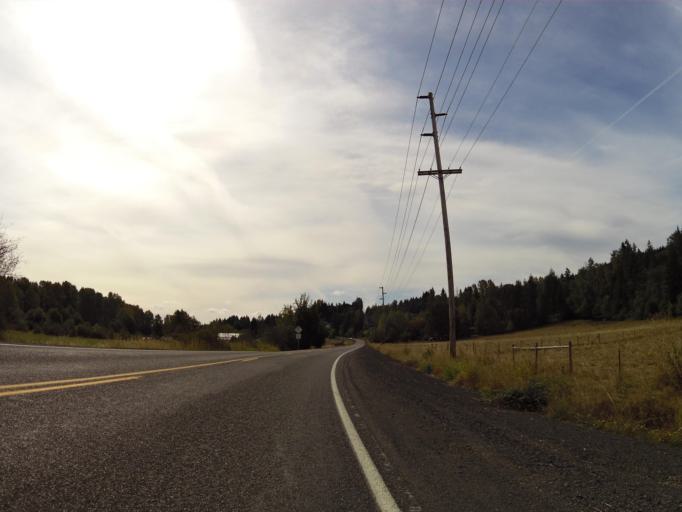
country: US
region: Washington
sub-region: Lewis County
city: Chehalis
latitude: 46.6403
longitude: -122.9713
